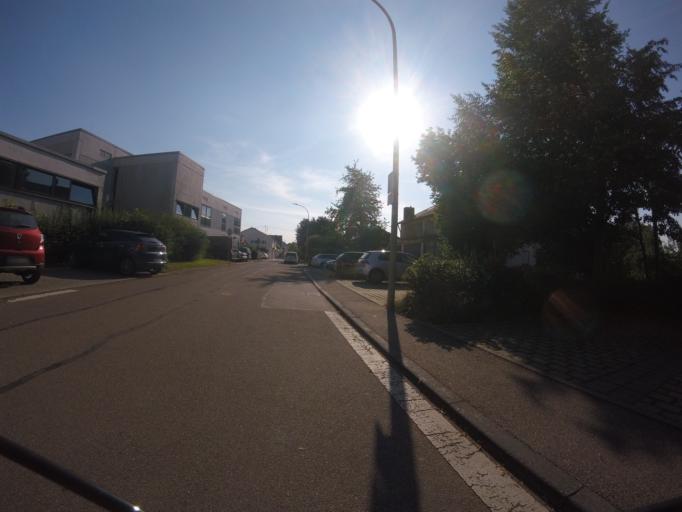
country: DE
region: Baden-Wuerttemberg
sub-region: Regierungsbezirk Stuttgart
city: Freiberg am Neckar
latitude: 48.9373
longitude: 9.2008
